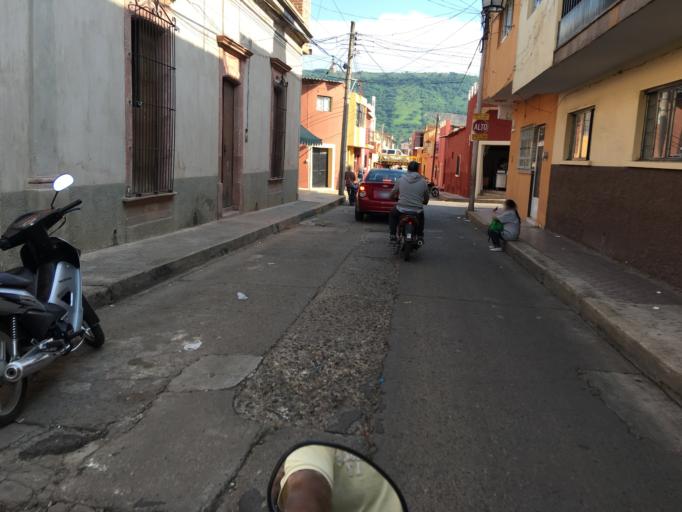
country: MX
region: Jalisco
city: Atotonilco el Alto
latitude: 20.5498
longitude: -102.5063
